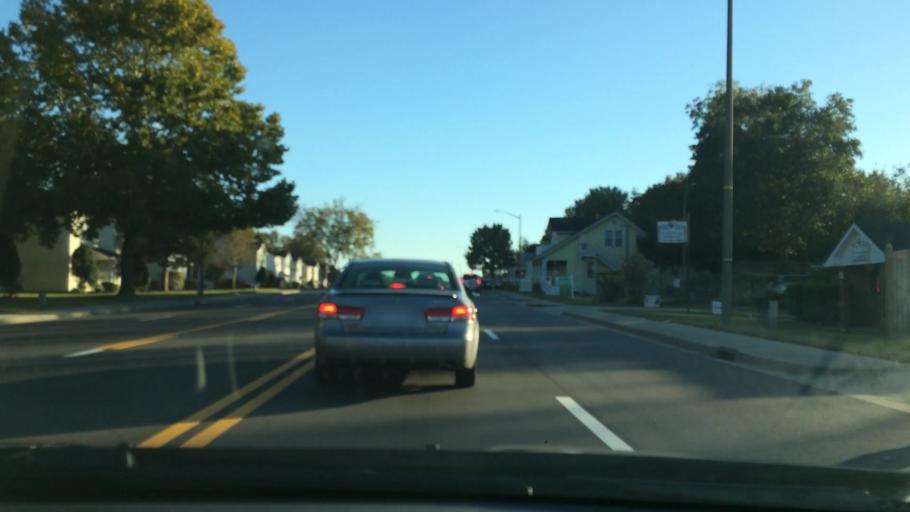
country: US
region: North Carolina
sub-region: Pitt County
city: Greenville
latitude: 35.6047
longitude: -77.3747
